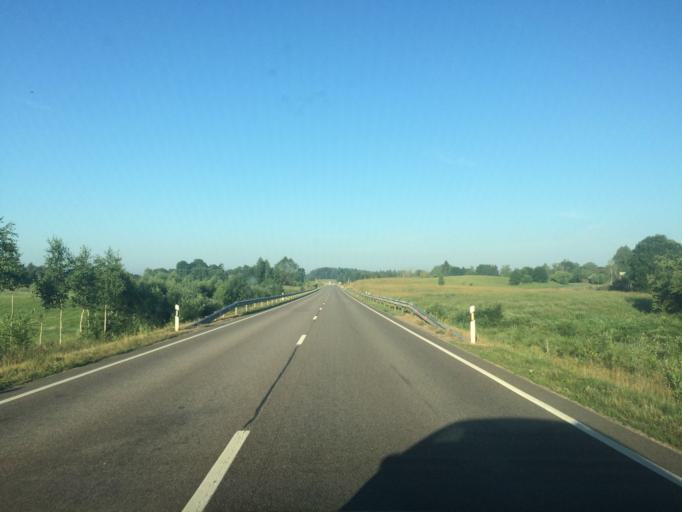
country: LT
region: Utenos apskritis
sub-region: Anyksciai
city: Anyksciai
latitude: 55.4161
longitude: 25.2113
